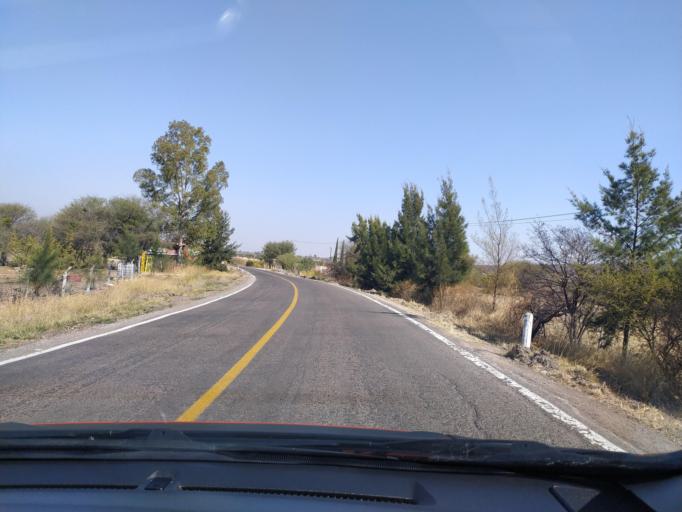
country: MX
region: Guanajuato
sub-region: San Francisco del Rincon
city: San Ignacio de Hidalgo
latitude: 20.8053
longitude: -101.8371
